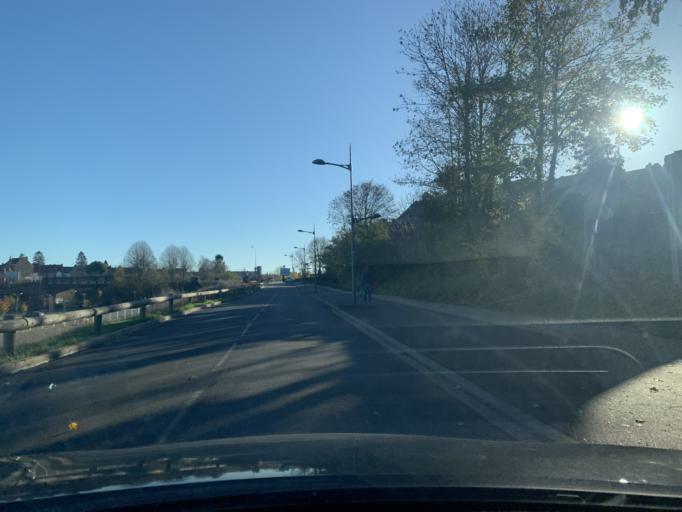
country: FR
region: Nord-Pas-de-Calais
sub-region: Departement du Nord
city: Cambrai
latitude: 50.1740
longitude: 3.2440
